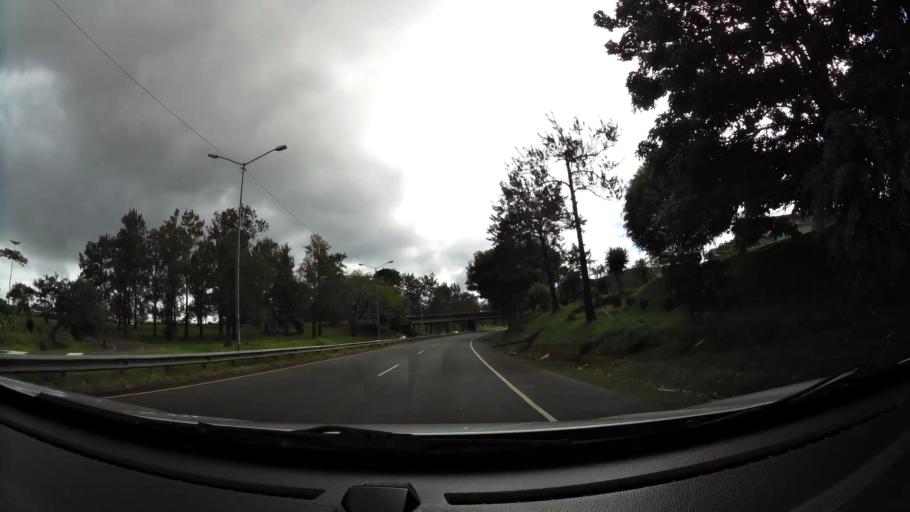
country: CR
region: San Jose
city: Curridabat
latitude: 9.9125
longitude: -84.0304
